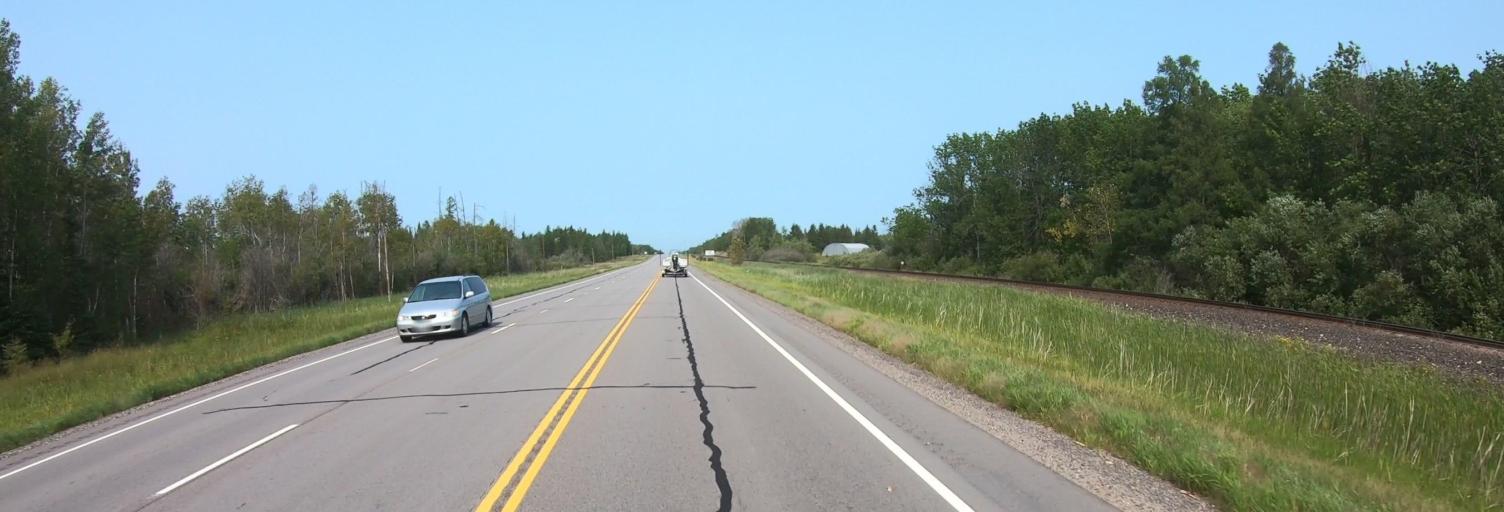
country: CA
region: Ontario
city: Fort Frances
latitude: 48.4421
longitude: -93.2579
